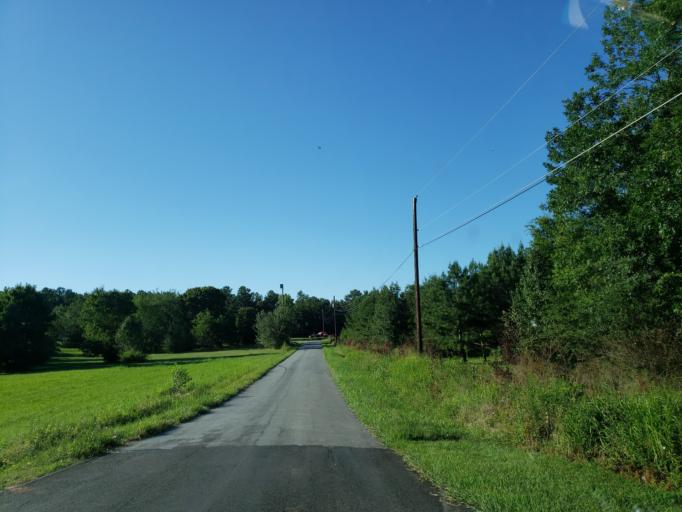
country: US
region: Georgia
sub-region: Bartow County
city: Euharlee
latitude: 34.1240
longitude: -85.0013
